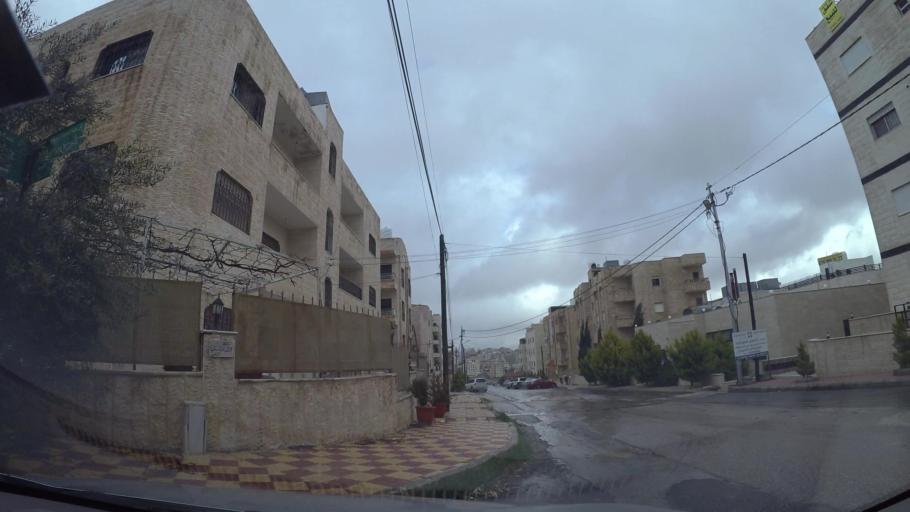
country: JO
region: Amman
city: Al Jubayhah
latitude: 32.0357
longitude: 35.8859
